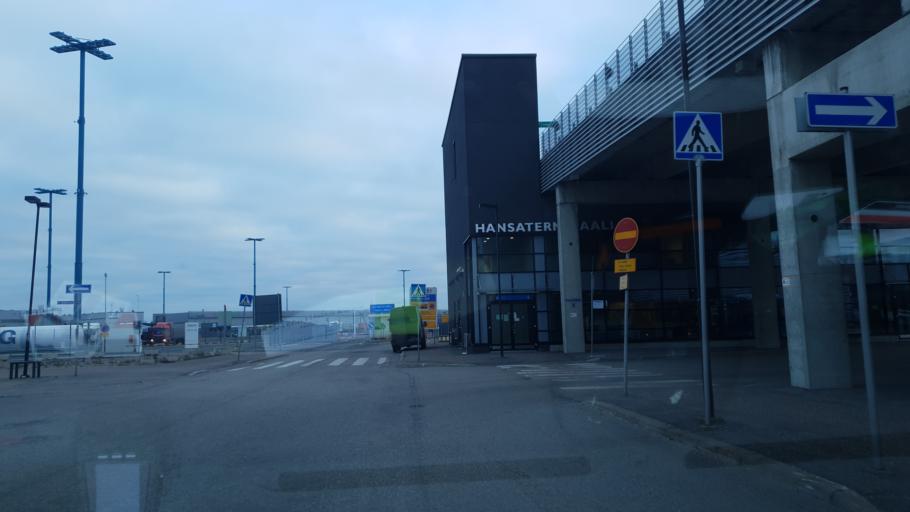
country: FI
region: Uusimaa
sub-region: Helsinki
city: Vantaa
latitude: 60.2218
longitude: 25.1750
